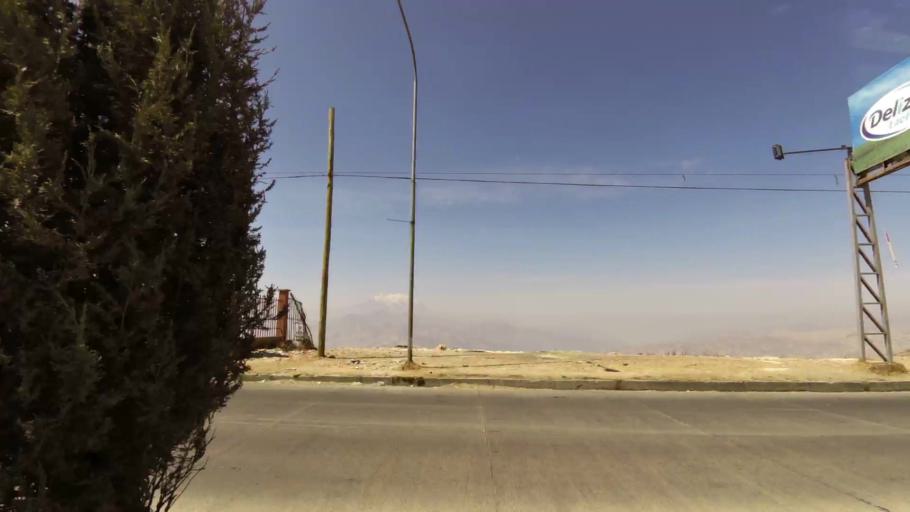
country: BO
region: La Paz
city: La Paz
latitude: -16.5305
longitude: -68.1474
